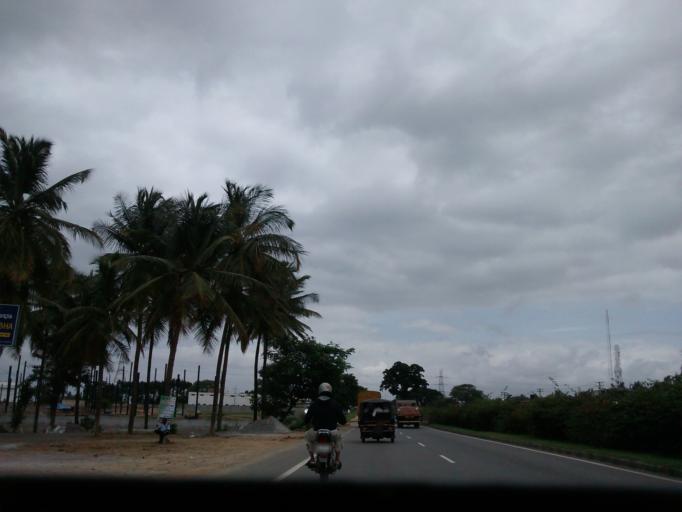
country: IN
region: Karnataka
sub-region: Bangalore Rural
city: Nelamangala
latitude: 13.1287
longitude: 77.3611
